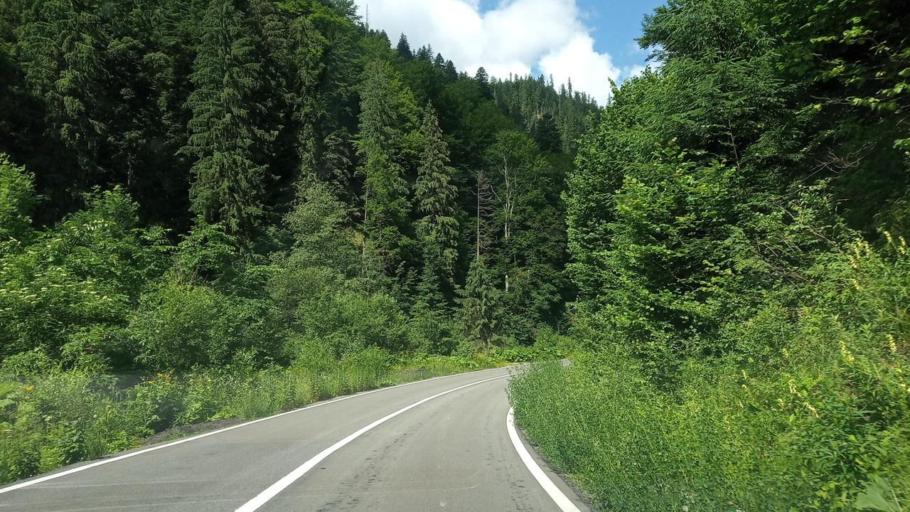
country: RO
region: Alba
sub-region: Comuna Sugag
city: Sugag
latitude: 45.6588
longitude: 23.6226
